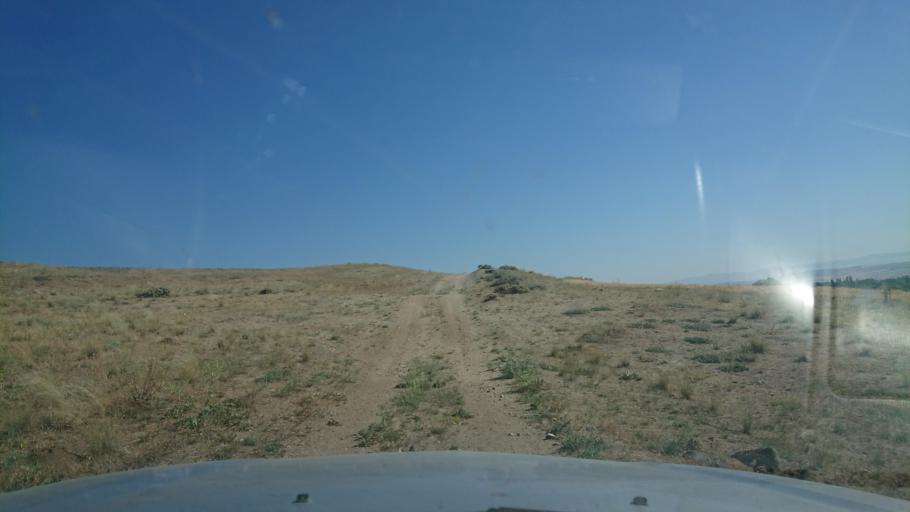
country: TR
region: Aksaray
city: Agacoren
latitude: 38.8463
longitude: 33.9266
